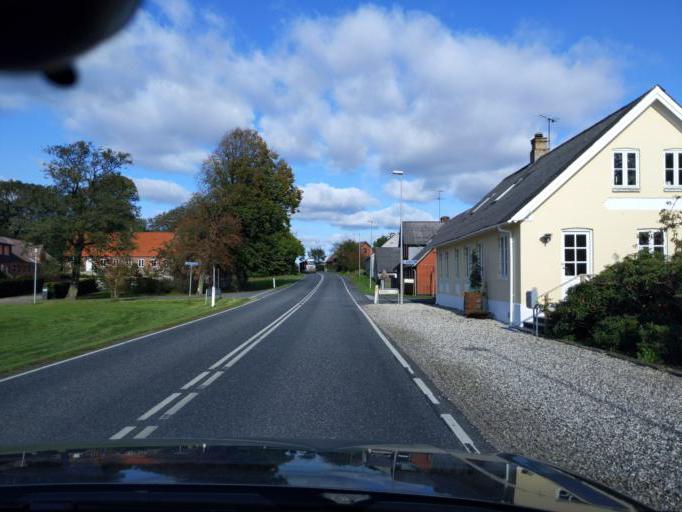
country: DK
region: Central Jutland
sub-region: Viborg Kommune
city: Bjerringbro
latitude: 56.4969
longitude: 9.5828
